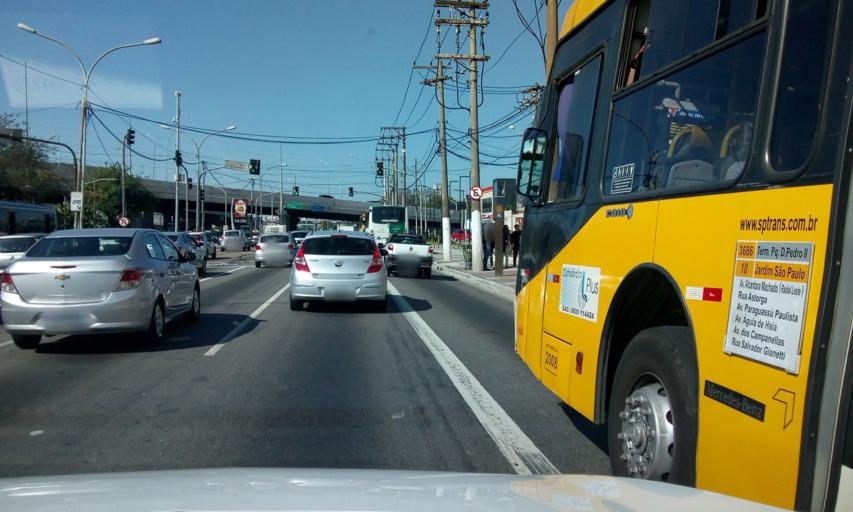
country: BR
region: Sao Paulo
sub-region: Sao Paulo
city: Sao Paulo
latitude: -23.5377
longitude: -46.5585
